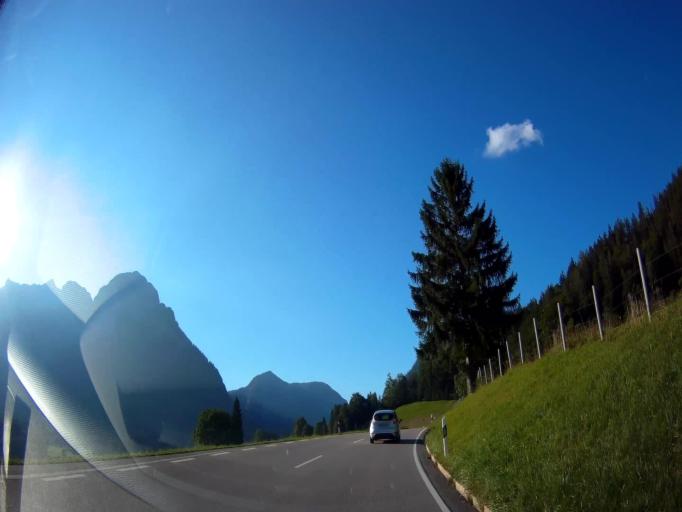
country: DE
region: Bavaria
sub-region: Upper Bavaria
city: Ramsau
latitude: 47.6172
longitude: 12.8824
